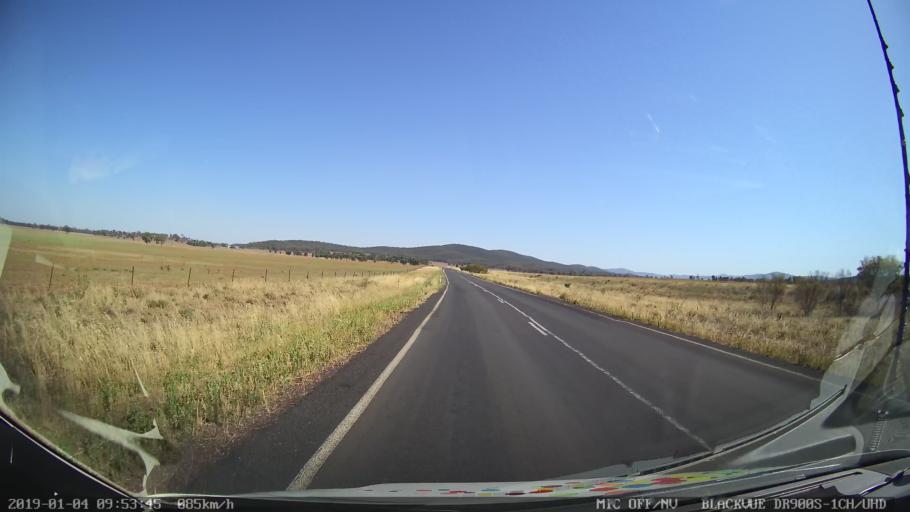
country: AU
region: New South Wales
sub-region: Cabonne
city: Canowindra
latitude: -33.5485
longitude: 148.4197
